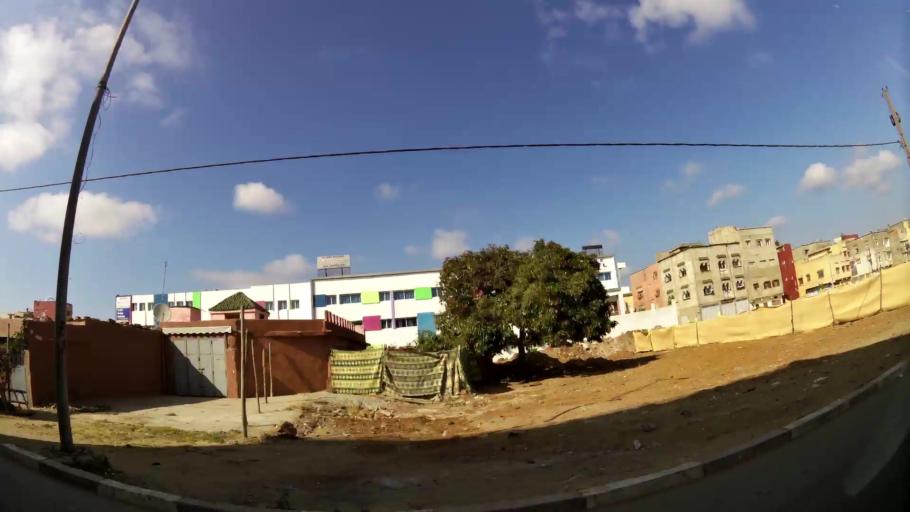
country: MA
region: Rabat-Sale-Zemmour-Zaer
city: Sale
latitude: 34.0608
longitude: -6.7698
